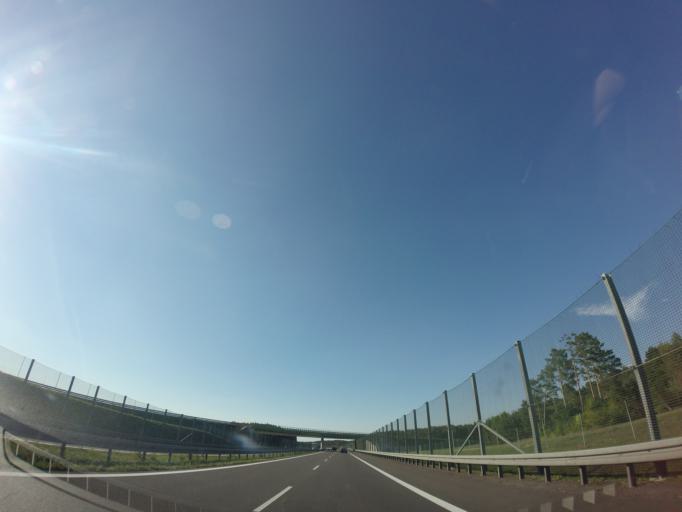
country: PL
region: Lubusz
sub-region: Powiat miedzyrzecki
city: Skwierzyna
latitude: 52.5689
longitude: 15.4721
